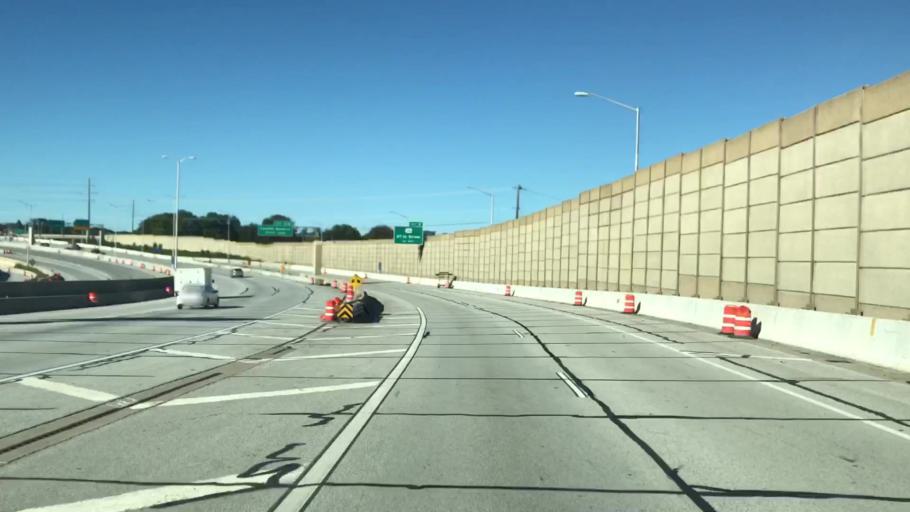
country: US
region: Wisconsin
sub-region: Milwaukee County
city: Saint Francis
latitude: 42.9661
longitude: -87.9299
